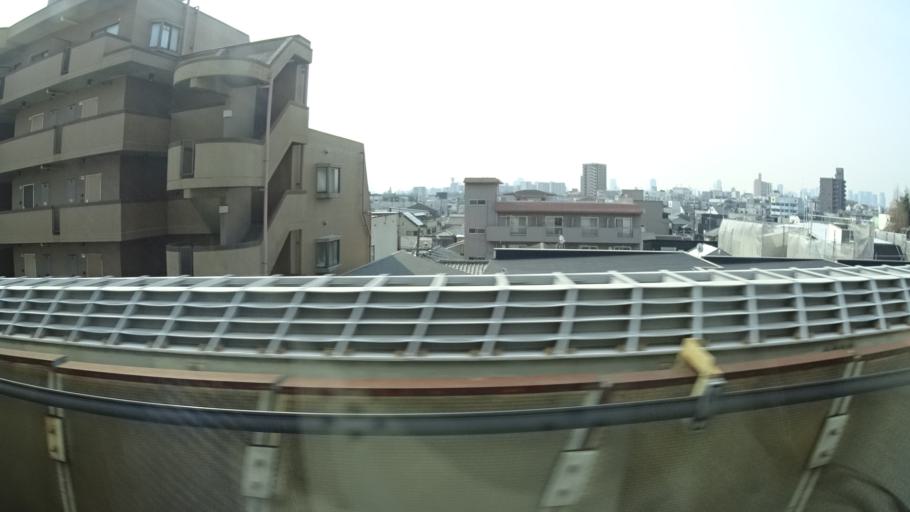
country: JP
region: Osaka
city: Suita
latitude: 34.7446
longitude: 135.5184
